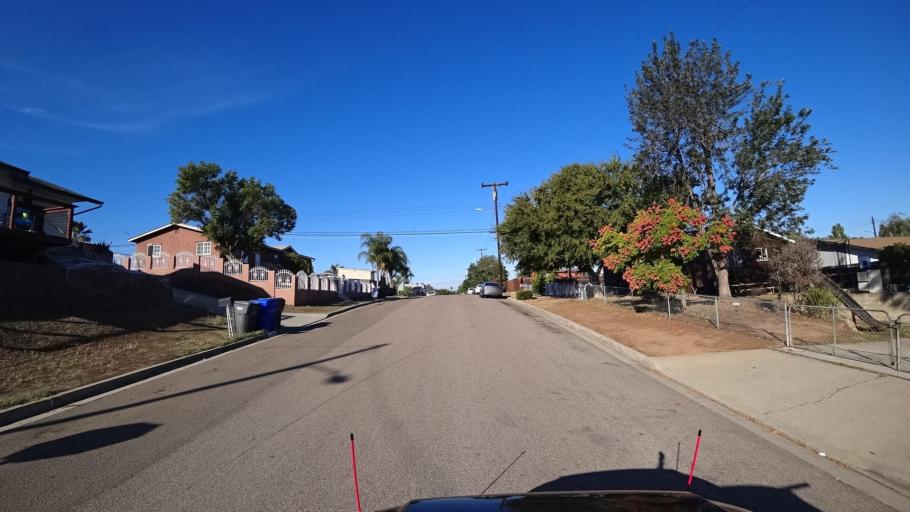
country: US
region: California
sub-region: San Diego County
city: La Presa
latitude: 32.7116
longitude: -116.9951
